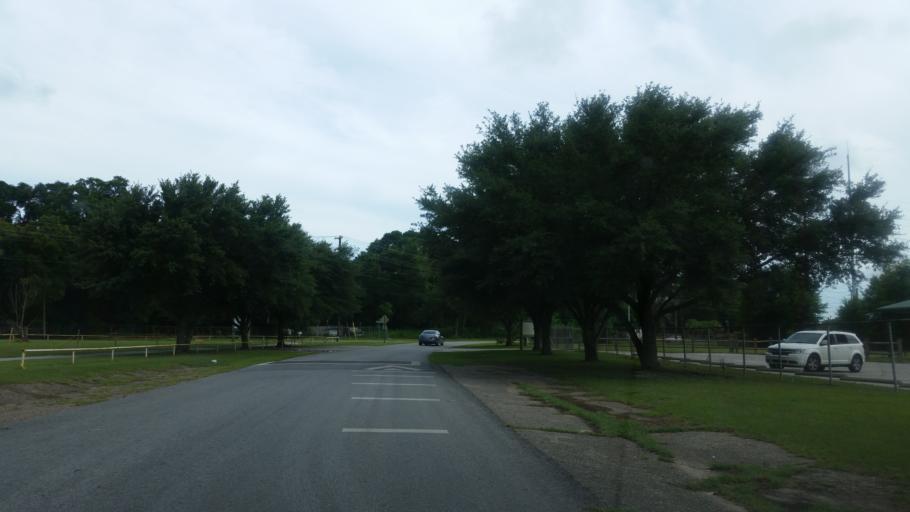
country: US
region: Florida
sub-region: Escambia County
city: Goulding
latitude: 30.4413
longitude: -87.2200
